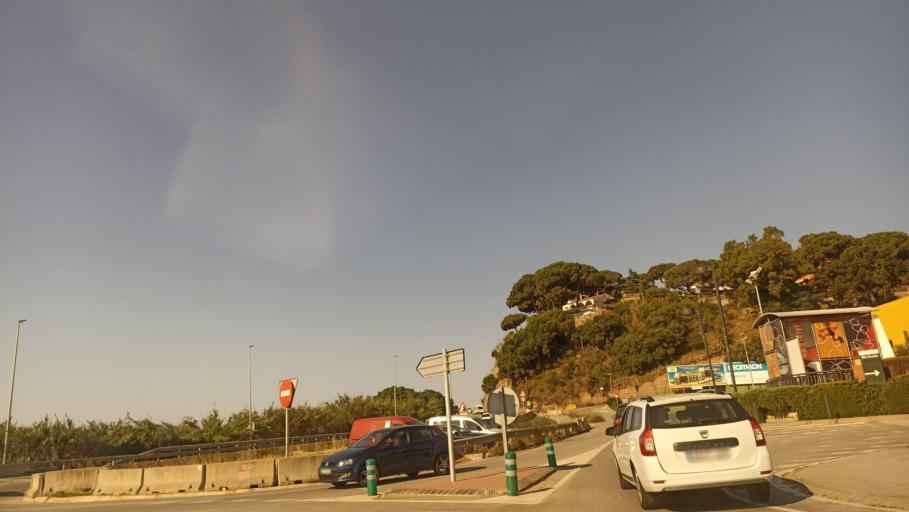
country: ES
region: Catalonia
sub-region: Provincia de Barcelona
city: Caldes d'Estrac
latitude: 41.5745
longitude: 2.5405
